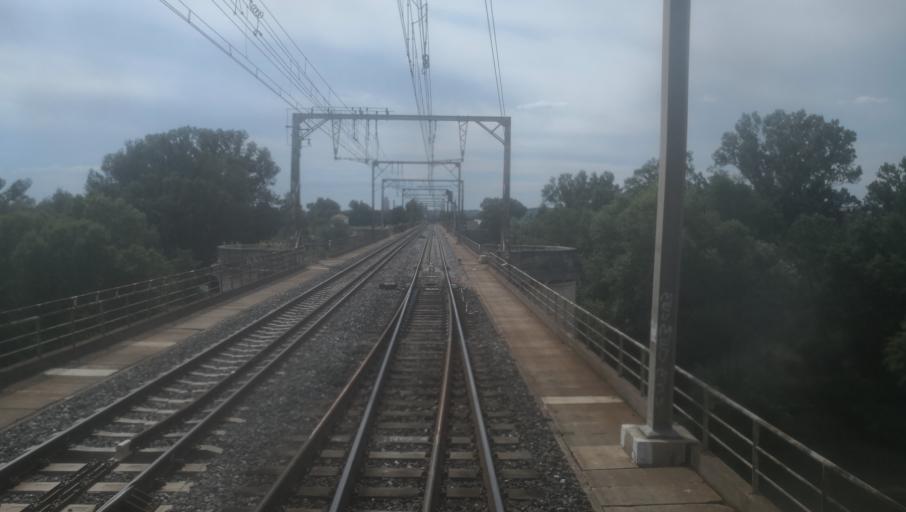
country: FR
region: Provence-Alpes-Cote d'Azur
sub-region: Departement des Bouches-du-Rhone
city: Tarascon
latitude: 43.8016
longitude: 4.6525
